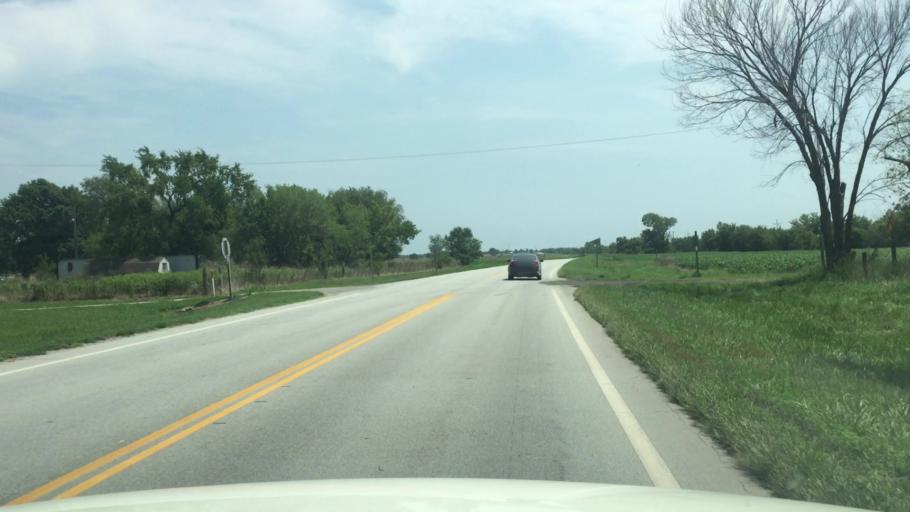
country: US
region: Kansas
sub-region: Cherokee County
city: Columbus
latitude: 37.1799
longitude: -94.9458
